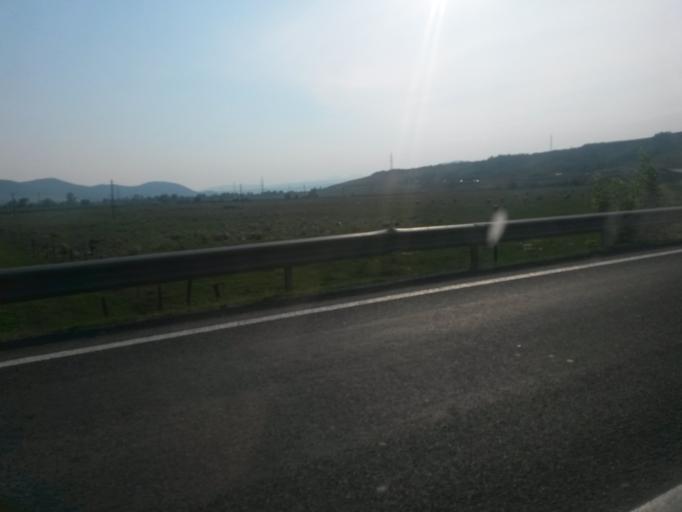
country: RO
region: Alba
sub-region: Comuna Unirea
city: Unirea
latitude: 46.3951
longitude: 23.8011
